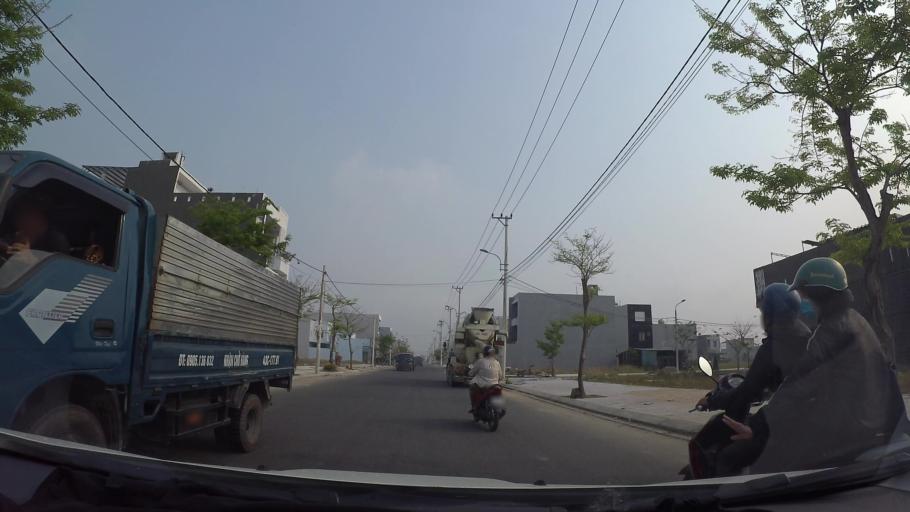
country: VN
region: Da Nang
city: Ngu Hanh Son
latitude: 16.0105
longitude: 108.2294
